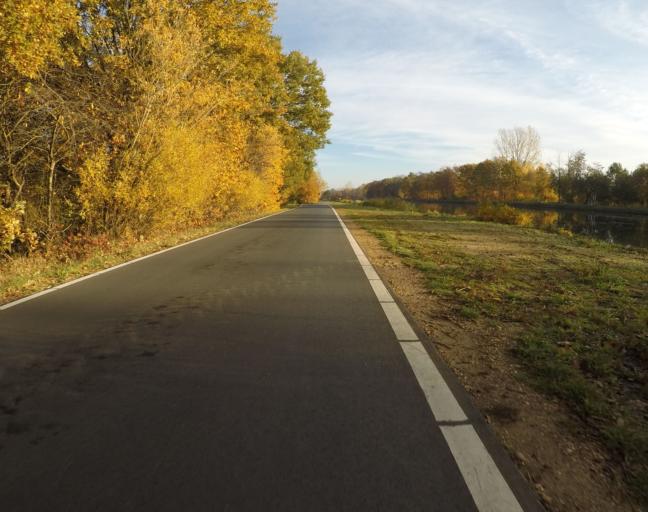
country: BE
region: Flanders
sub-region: Provincie Antwerpen
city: Geel
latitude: 51.1914
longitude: 4.9565
